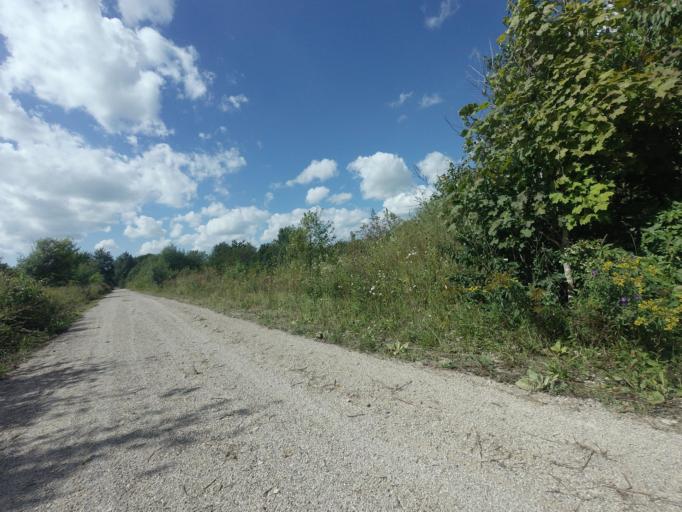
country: CA
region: Ontario
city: Huron East
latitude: 43.7150
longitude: -81.3841
